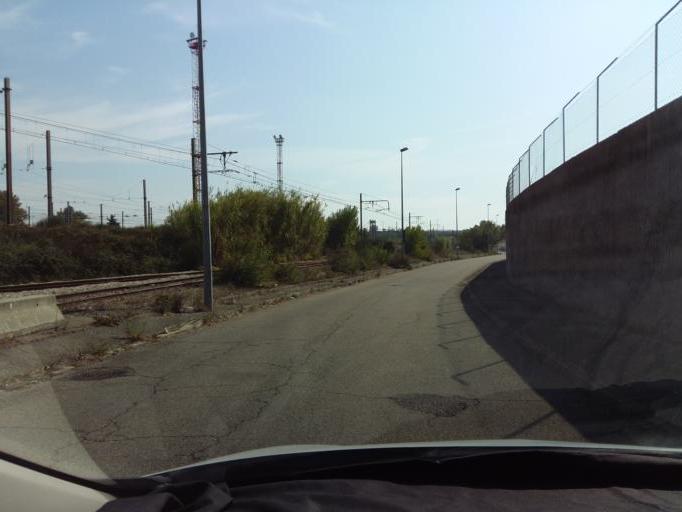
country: FR
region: Provence-Alpes-Cote d'Azur
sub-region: Departement du Vaucluse
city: Avignon
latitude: 43.9291
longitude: 4.7938
